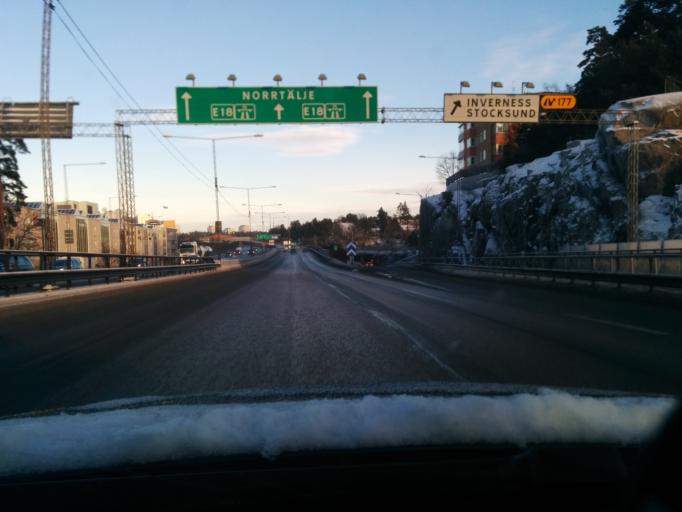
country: SE
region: Stockholm
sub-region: Norrtalje Kommun
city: Bergshamra
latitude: 59.3836
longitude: 18.0422
